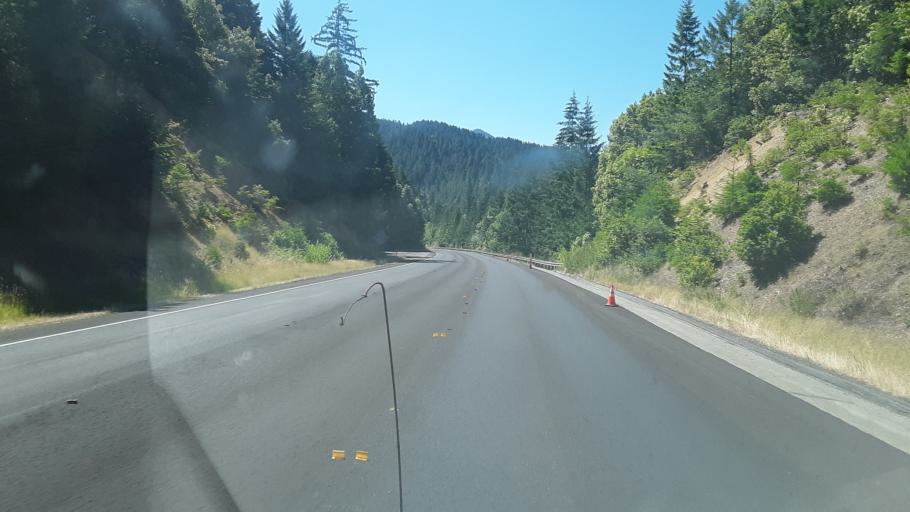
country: US
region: Oregon
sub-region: Josephine County
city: Cave Junction
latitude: 41.9611
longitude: -123.7462
